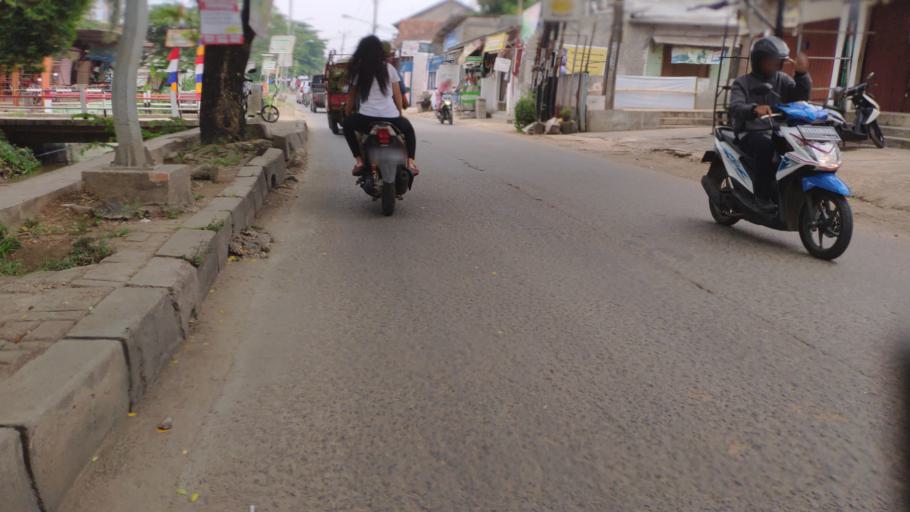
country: ID
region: West Java
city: Sawangan
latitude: -6.3854
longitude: 106.7912
